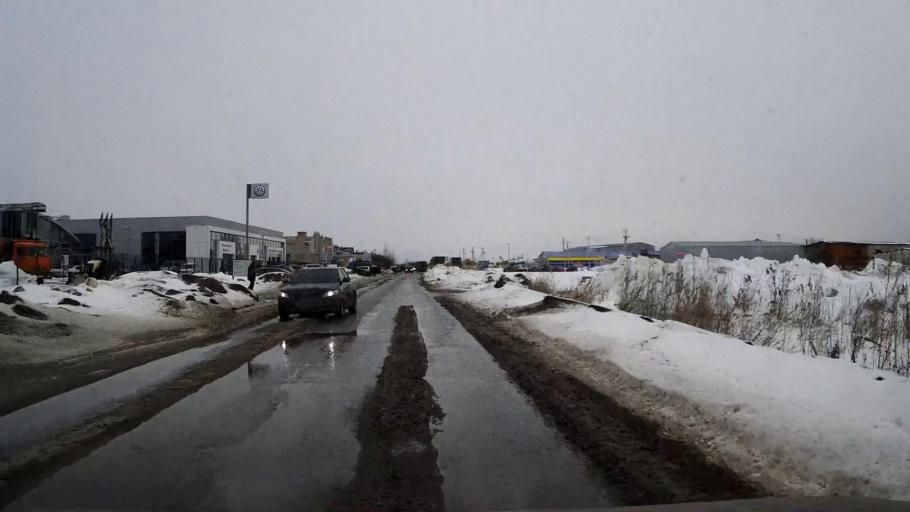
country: RU
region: Vologda
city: Vologda
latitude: 59.2195
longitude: 39.9446
